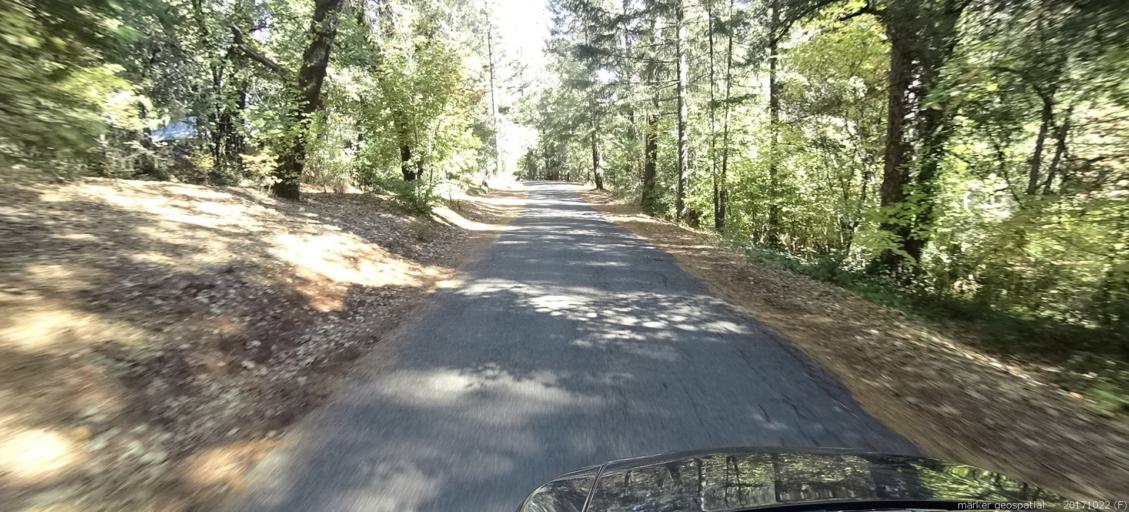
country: US
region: California
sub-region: Shasta County
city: Central Valley (historical)
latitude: 40.9375
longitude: -122.4516
